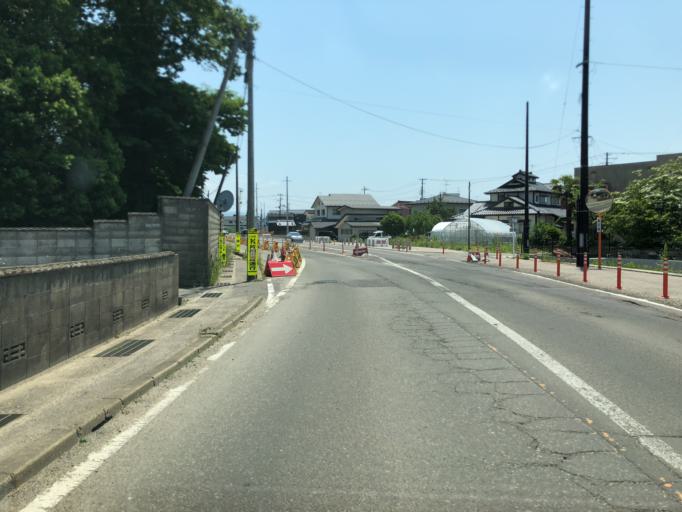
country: JP
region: Fukushima
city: Yanagawamachi-saiwaicho
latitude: 37.8615
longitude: 140.6078
